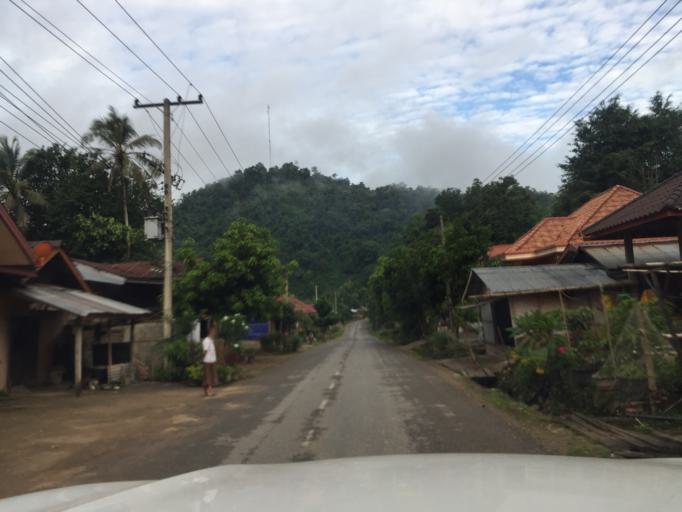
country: LA
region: Phongsali
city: Khoa
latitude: 21.1018
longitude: 102.2599
